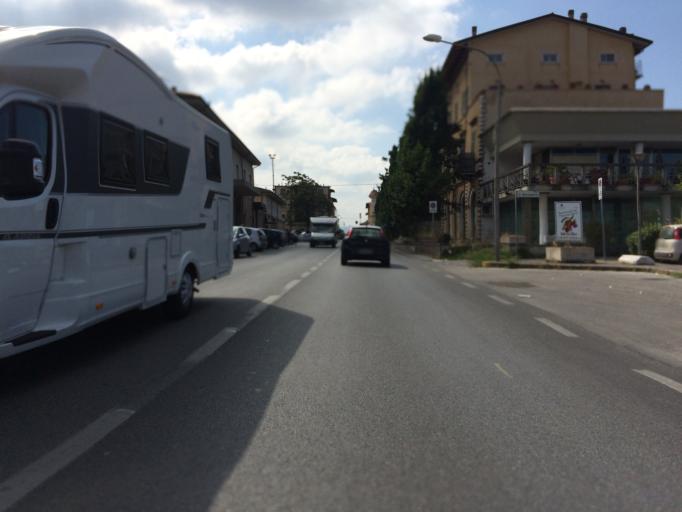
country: IT
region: Tuscany
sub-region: Provincia di Lucca
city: Ripa-Pozzi-Querceta-Ponterosso
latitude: 43.9782
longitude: 10.1984
